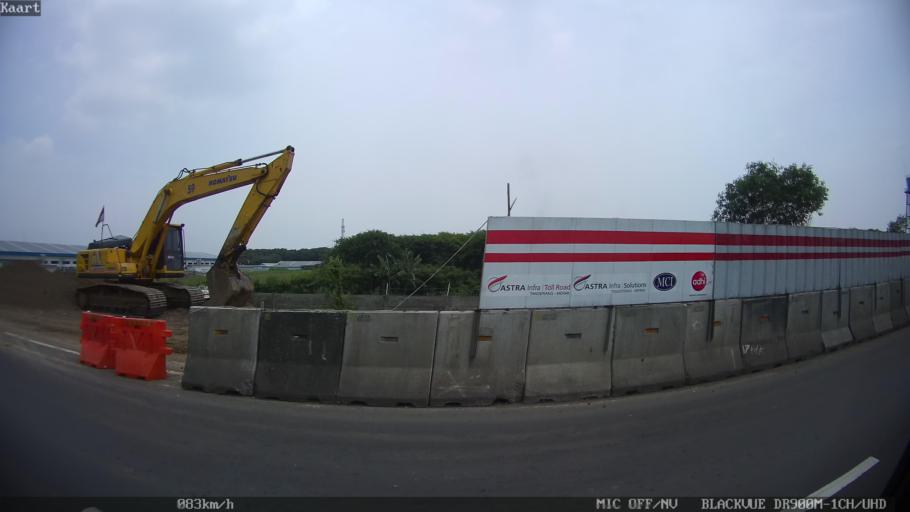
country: ID
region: West Java
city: Kresek
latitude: -6.1661
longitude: 106.3361
